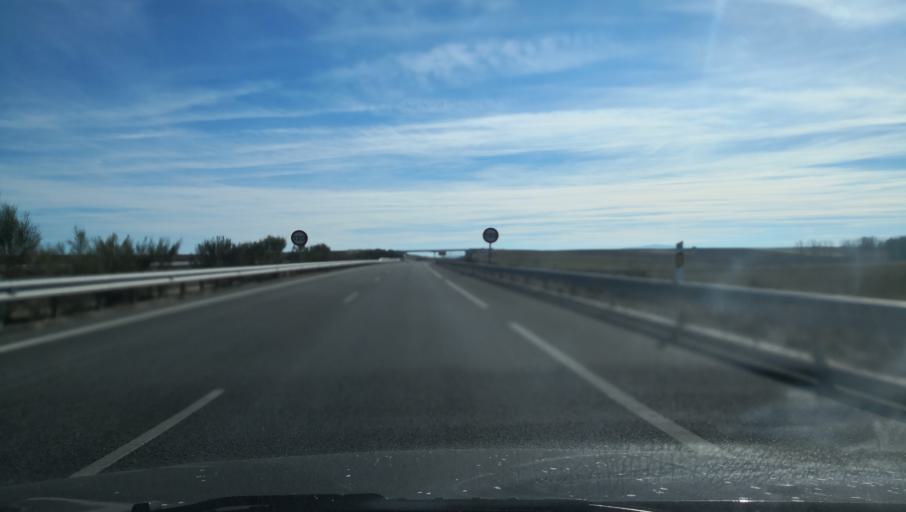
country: ES
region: Castille and Leon
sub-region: Provincia de Avila
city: Gimialcon
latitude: 40.8843
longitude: -5.1436
